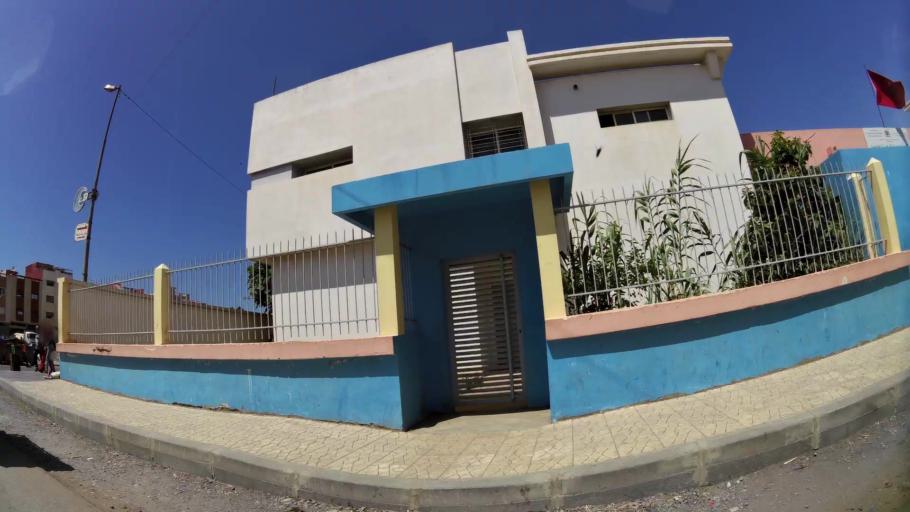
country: MA
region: Rabat-Sale-Zemmour-Zaer
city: Sale
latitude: 34.0641
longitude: -6.7802
